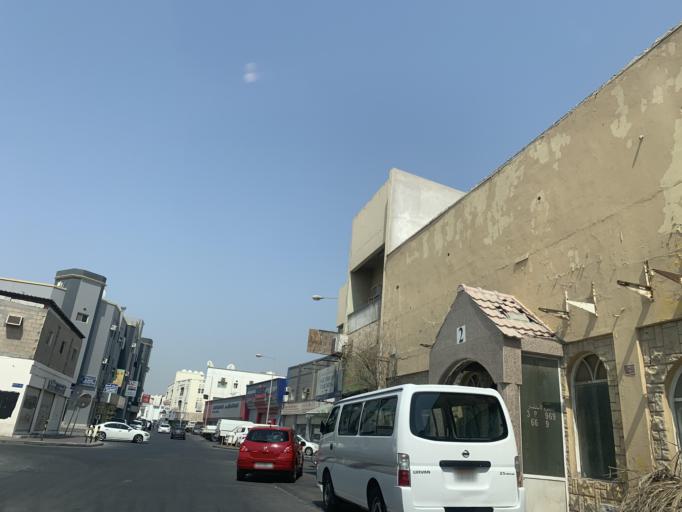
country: BH
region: Manama
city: Jidd Hafs
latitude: 26.2032
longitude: 50.5315
